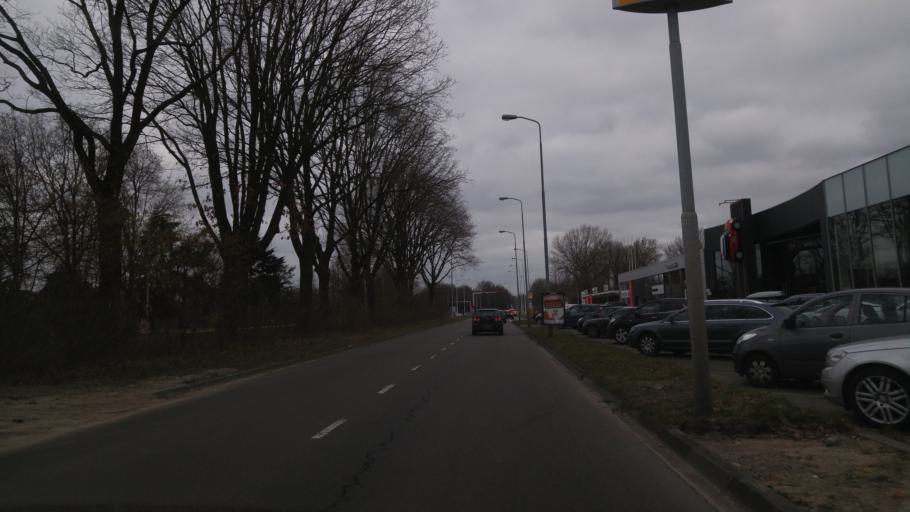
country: NL
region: North Brabant
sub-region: Gemeente Eindhoven
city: Eindhoven
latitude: 51.4809
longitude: 5.4554
